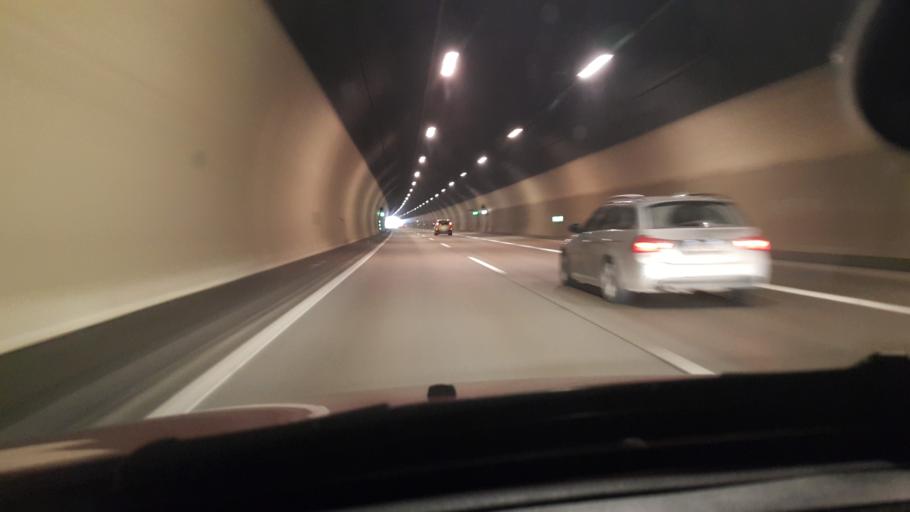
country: AT
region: Styria
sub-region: Politischer Bezirk Graz-Umgebung
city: Gratkorn
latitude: 47.1247
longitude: 15.3664
